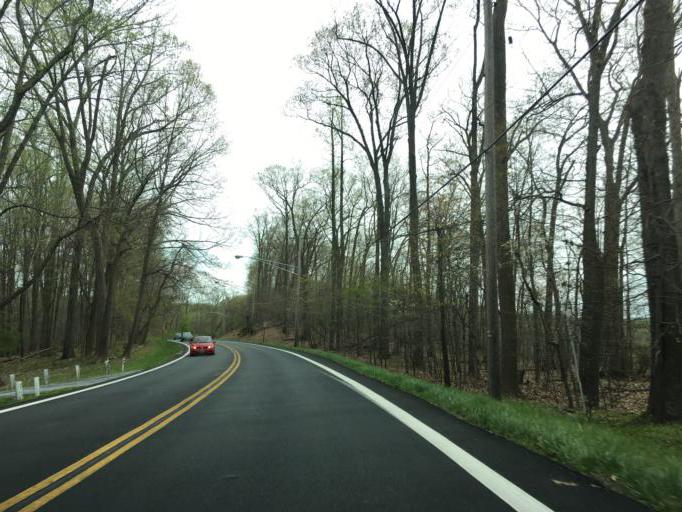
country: US
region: Maryland
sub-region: Baltimore County
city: Hampton
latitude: 39.4759
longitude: -76.5745
